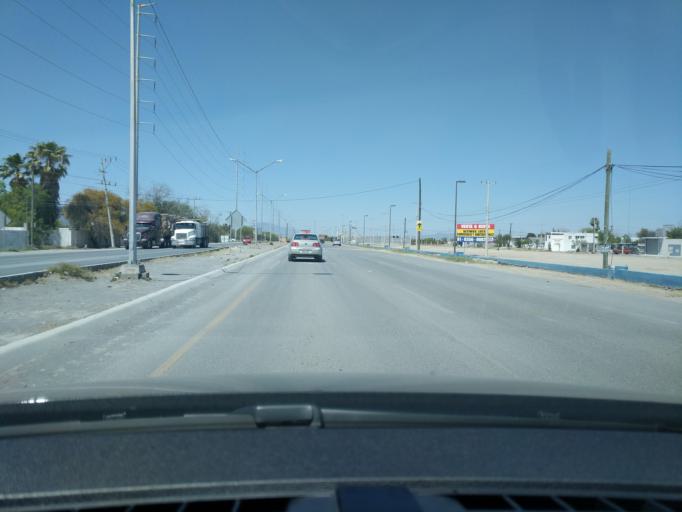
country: MX
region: Nuevo Leon
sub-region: Salinas Victoria
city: Emiliano Zapata
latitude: 25.9142
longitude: -100.2683
